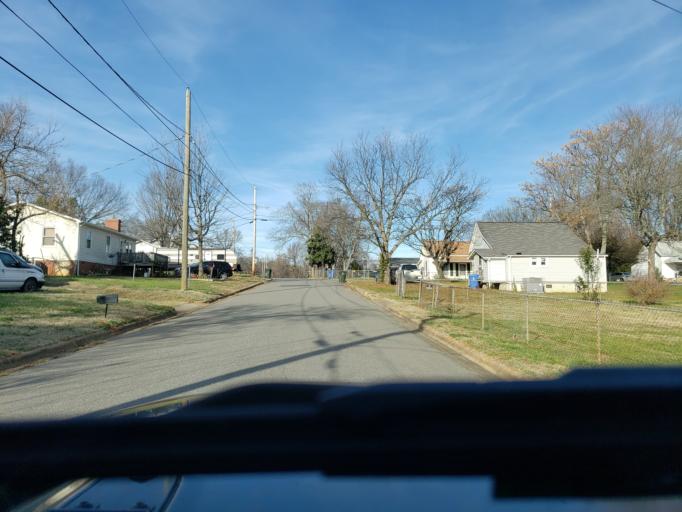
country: US
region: North Carolina
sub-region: Cleveland County
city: Kings Mountain
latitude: 35.2467
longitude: -81.3346
